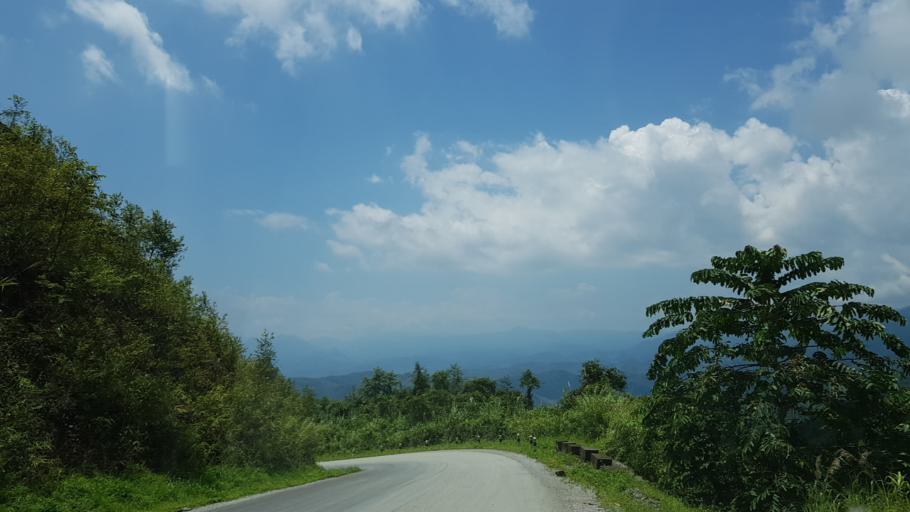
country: LA
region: Vientiane
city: Muang Kasi
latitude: 19.3823
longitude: 102.1538
